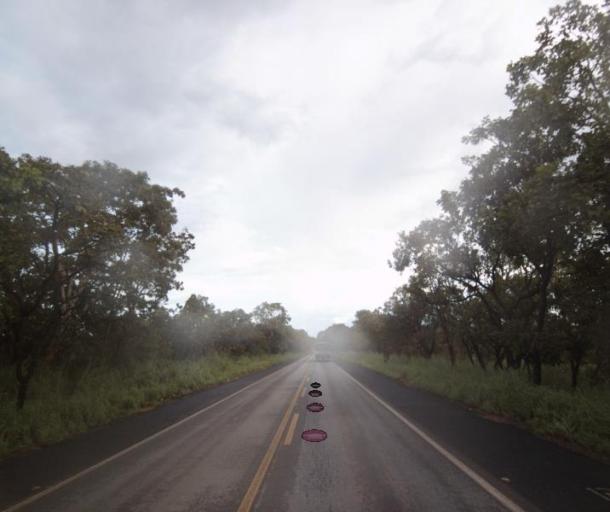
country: BR
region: Goias
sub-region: Porangatu
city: Porangatu
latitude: -13.9040
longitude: -49.0620
